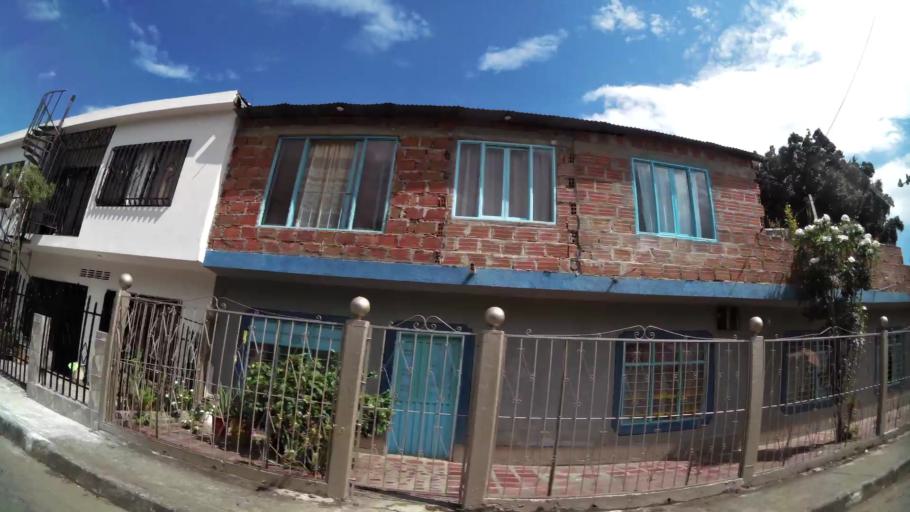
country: CO
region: Valle del Cauca
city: Cali
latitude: 3.4020
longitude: -76.5146
